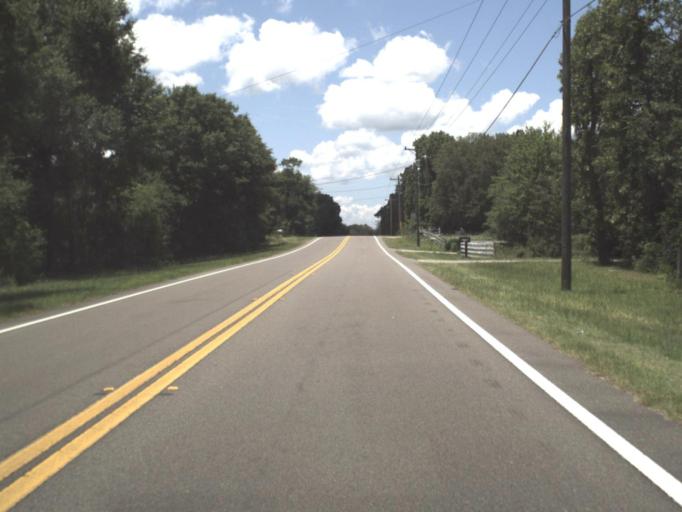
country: US
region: Florida
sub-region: Clay County
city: Keystone Heights
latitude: 29.7225
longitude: -81.9947
